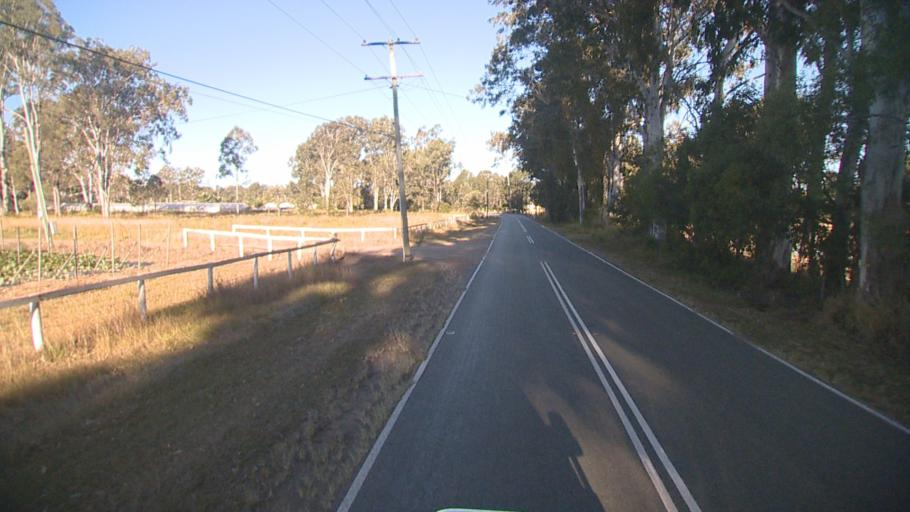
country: AU
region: Queensland
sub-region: Logan
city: Chambers Flat
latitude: -27.7522
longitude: 153.0798
